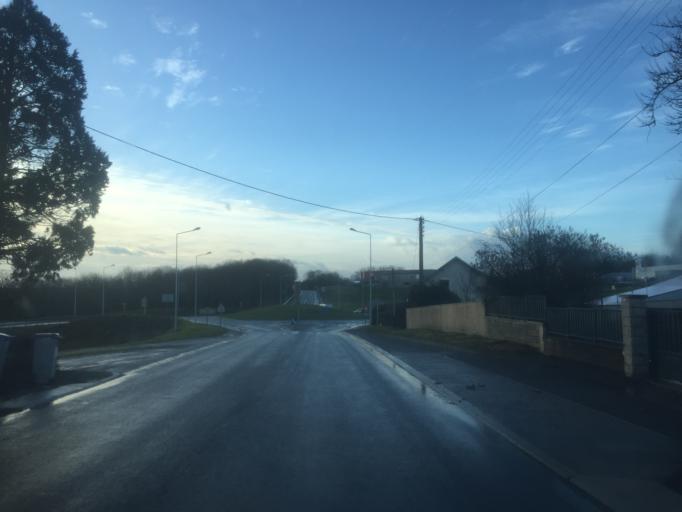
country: FR
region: Franche-Comte
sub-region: Departement du Jura
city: Dampierre
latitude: 47.1512
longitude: 5.7201
